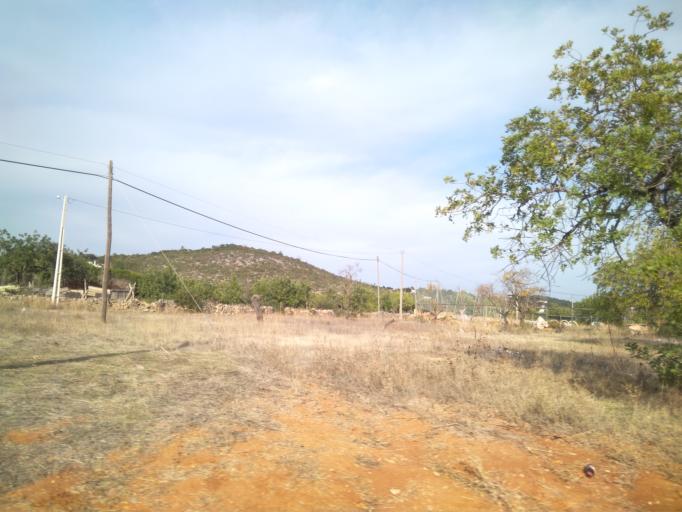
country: PT
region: Faro
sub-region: Faro
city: Santa Barbara de Nexe
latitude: 37.1042
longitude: -7.9567
